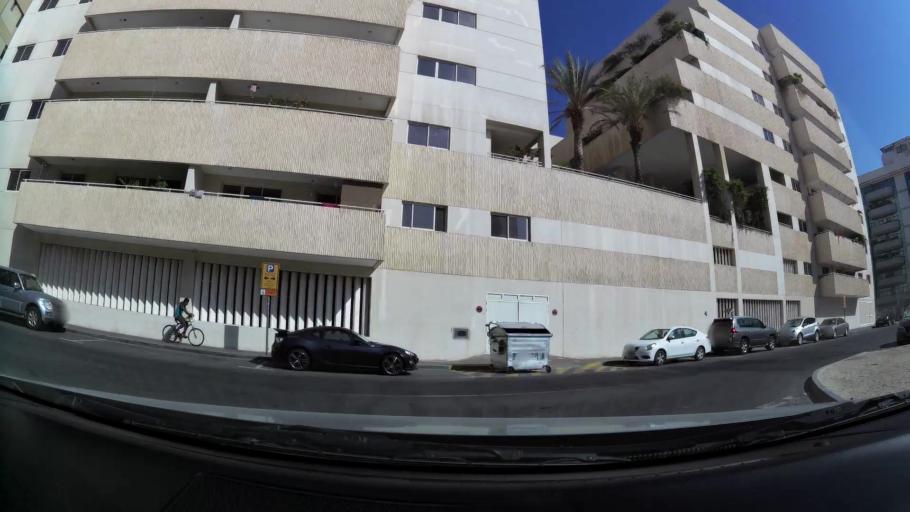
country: AE
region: Ash Shariqah
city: Sharjah
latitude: 25.2518
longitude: 55.2971
